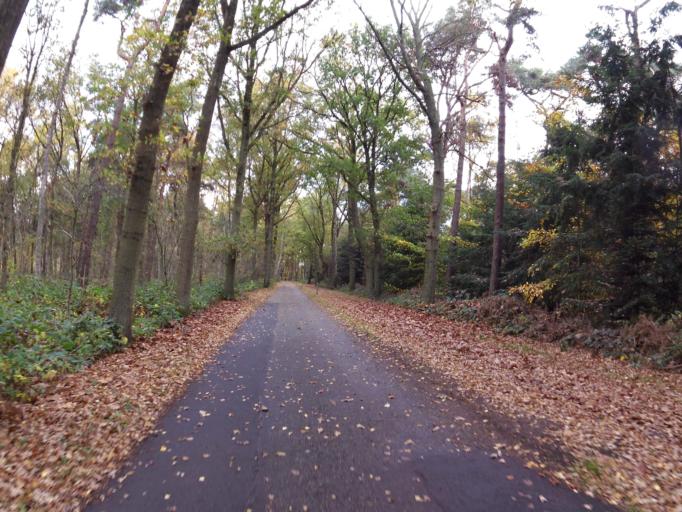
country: NL
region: North Brabant
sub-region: Gemeente Vught
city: Vught
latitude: 51.6491
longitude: 5.2485
